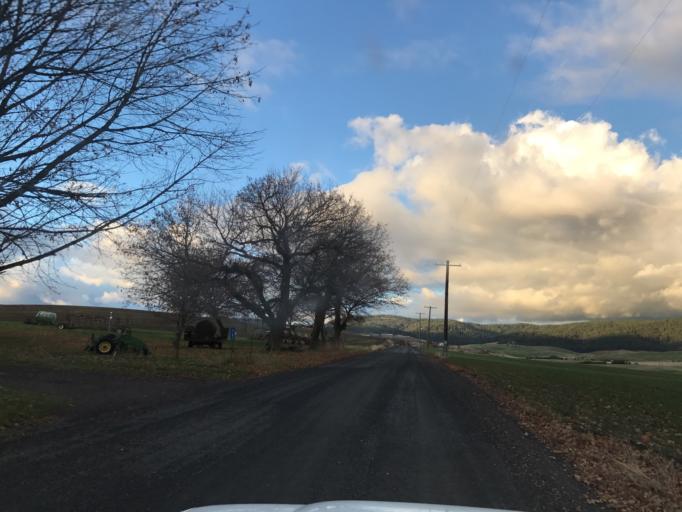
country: US
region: Idaho
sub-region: Latah County
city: Moscow
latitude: 46.7707
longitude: -116.9807
